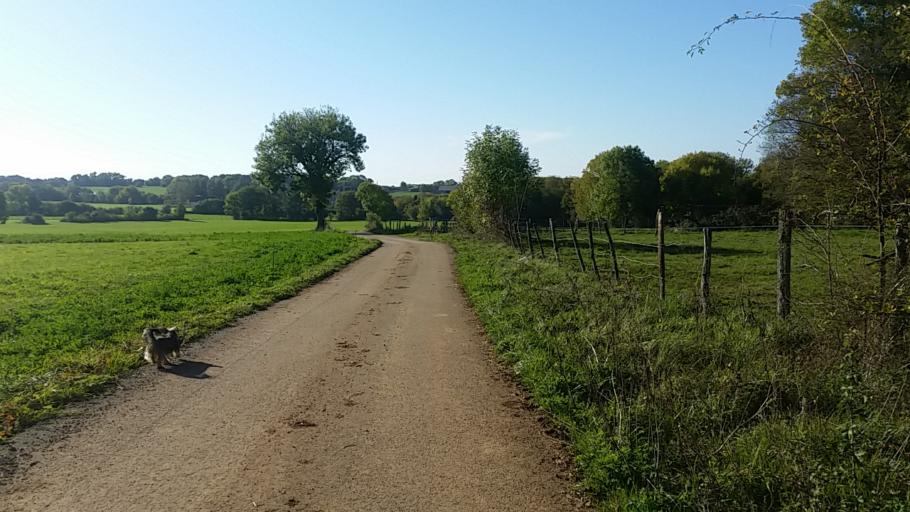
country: FR
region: Franche-Comte
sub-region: Departement du Doubs
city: Ornans
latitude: 47.0486
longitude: 6.0730
